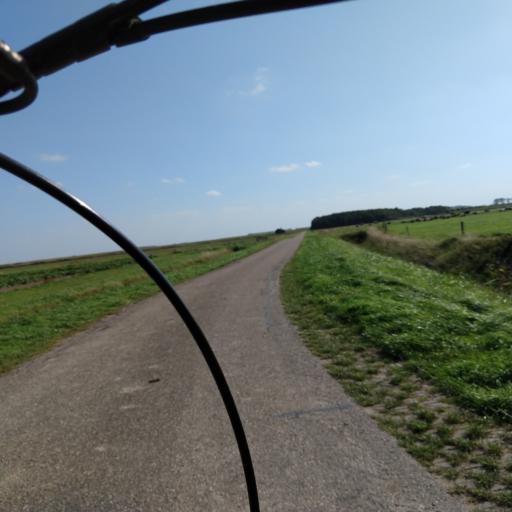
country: NL
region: Zeeland
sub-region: Gemeente Goes
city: Goes
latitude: 51.5667
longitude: 3.8896
